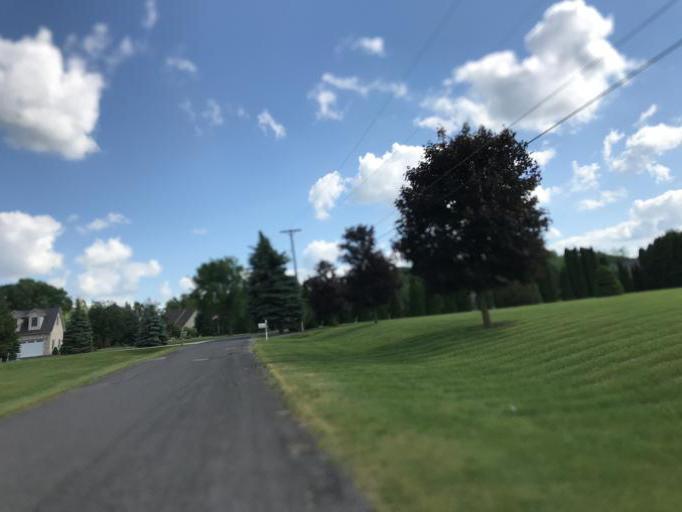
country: US
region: Michigan
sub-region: Oakland County
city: South Lyon
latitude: 42.4285
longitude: -83.6585
